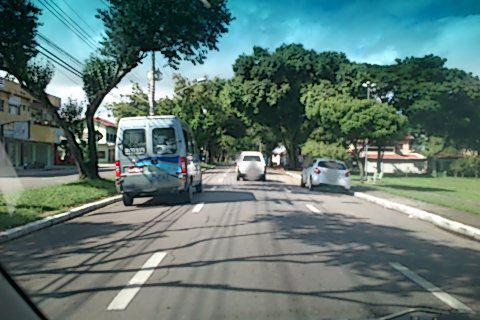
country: BR
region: Sao Paulo
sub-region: Sao Jose Dos Campos
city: Sao Jose dos Campos
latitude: -23.2310
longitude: -45.8804
